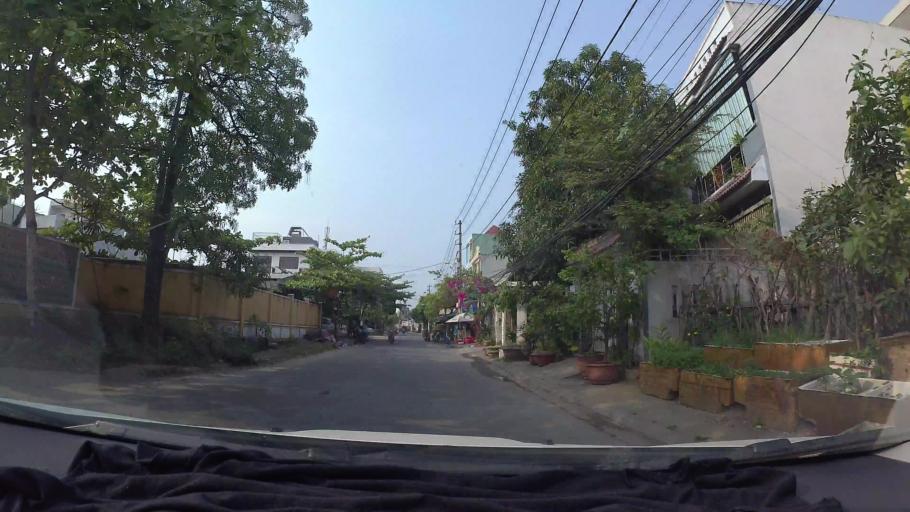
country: VN
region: Da Nang
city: Lien Chieu
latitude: 16.0544
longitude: 108.1669
